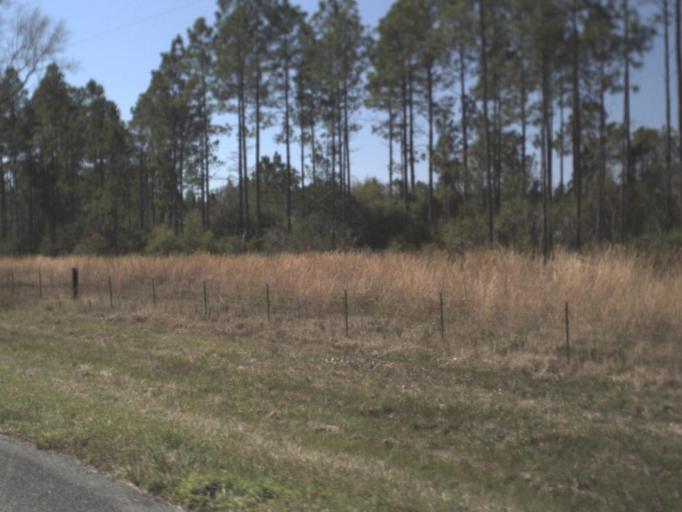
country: US
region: Florida
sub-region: Leon County
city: Woodville
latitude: 30.1981
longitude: -84.0501
